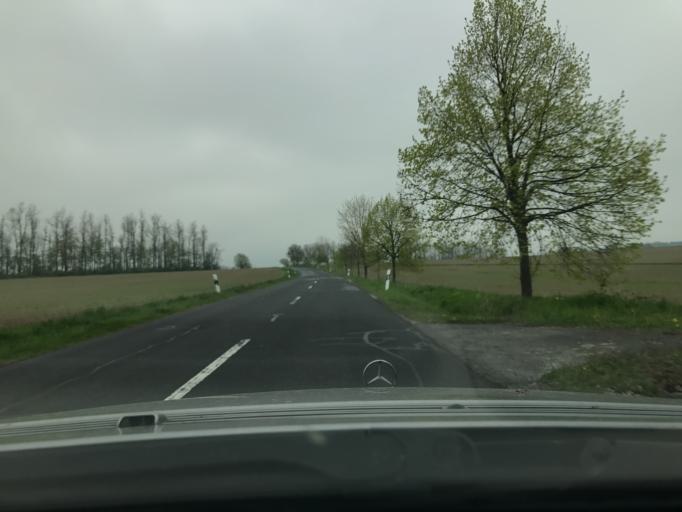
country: DE
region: Thuringia
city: Kreuzebra
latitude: 51.3329
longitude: 10.2660
